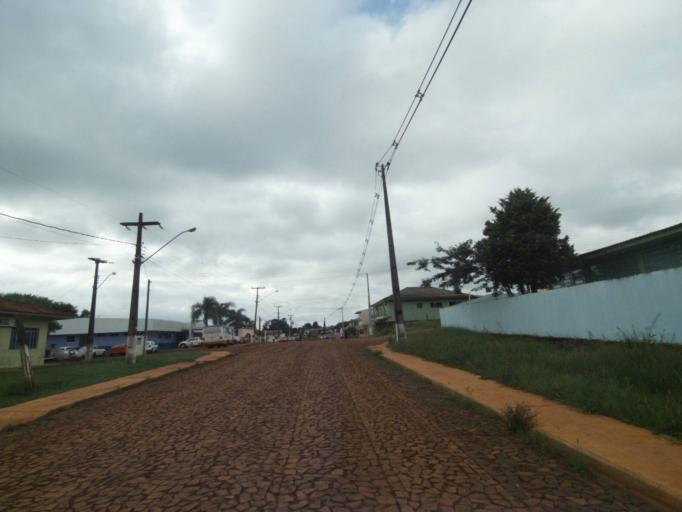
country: BR
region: Parana
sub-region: Pitanga
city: Pitanga
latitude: -24.9379
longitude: -51.8693
